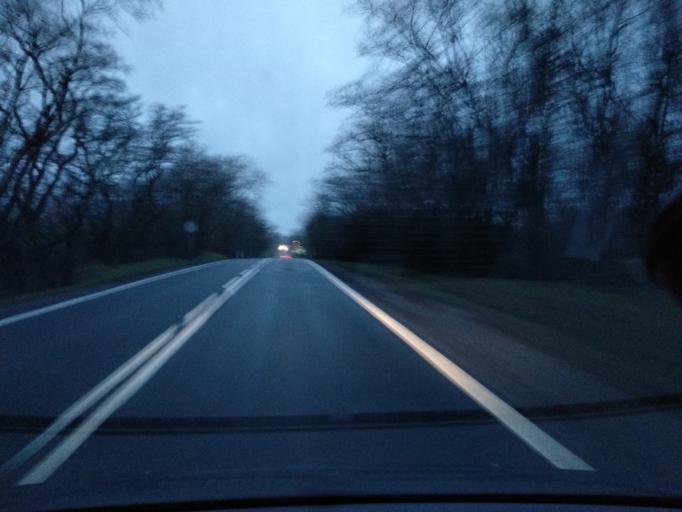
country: PL
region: Lower Silesian Voivodeship
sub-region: Powiat sredzki
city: Malczyce
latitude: 51.2231
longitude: 16.4410
